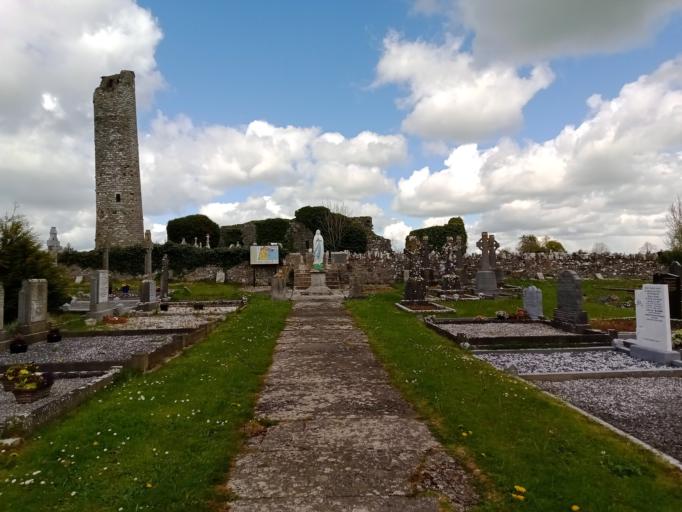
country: IE
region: Leinster
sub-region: Kilkenny
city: Thomastown
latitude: 52.5789
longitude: -7.1294
